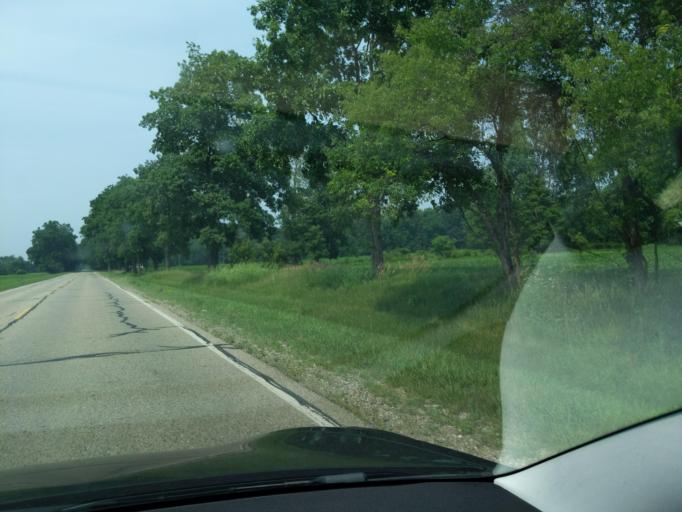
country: US
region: Michigan
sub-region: Ingham County
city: Edgemont Park
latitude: 42.7864
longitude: -84.5693
